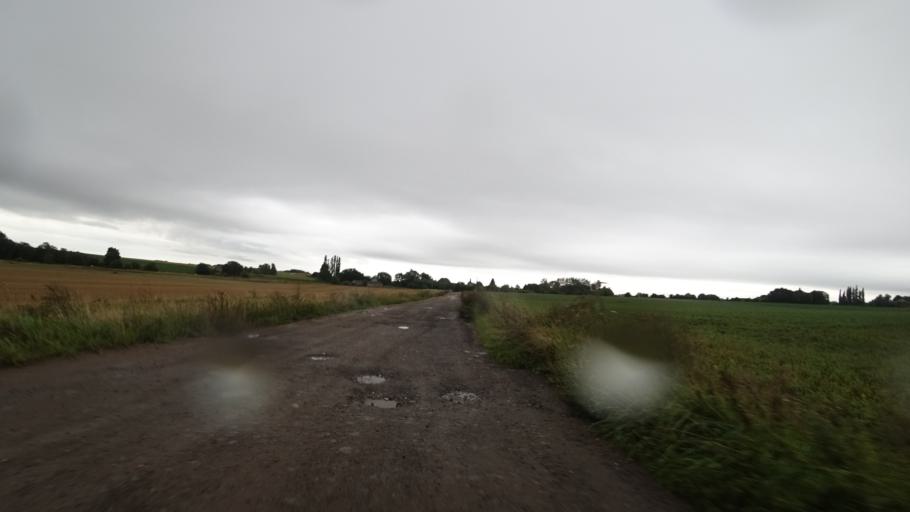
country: BE
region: Wallonia
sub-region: Province de Namur
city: Gembloux
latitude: 50.5713
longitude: 4.7320
